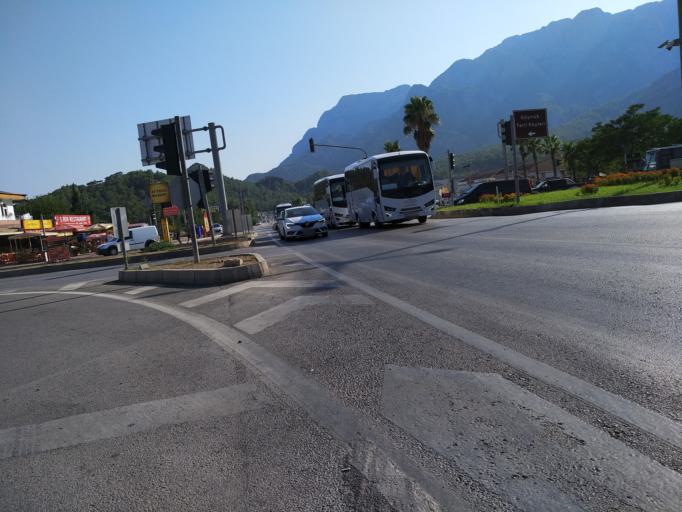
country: TR
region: Antalya
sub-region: Kemer
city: Goeynuek
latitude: 36.6668
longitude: 30.5520
